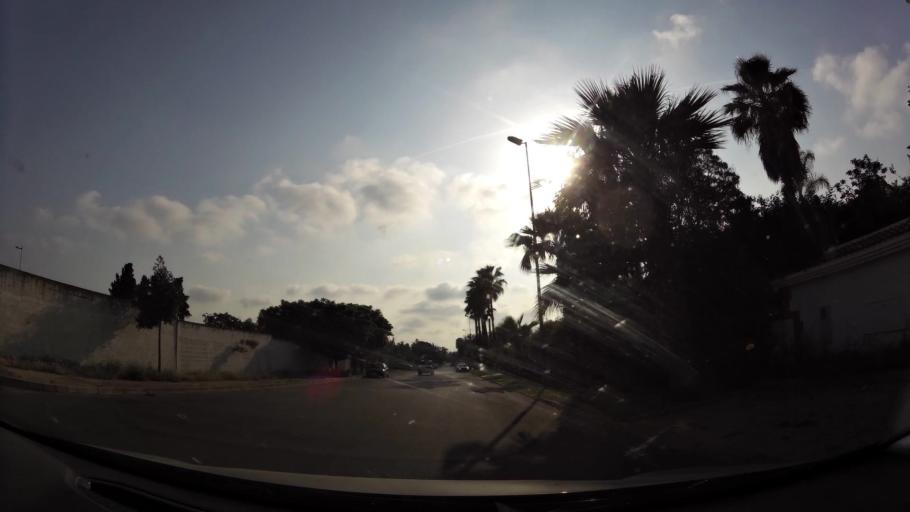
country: MA
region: Rabat-Sale-Zemmour-Zaer
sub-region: Rabat
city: Rabat
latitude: 33.9435
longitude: -6.8166
